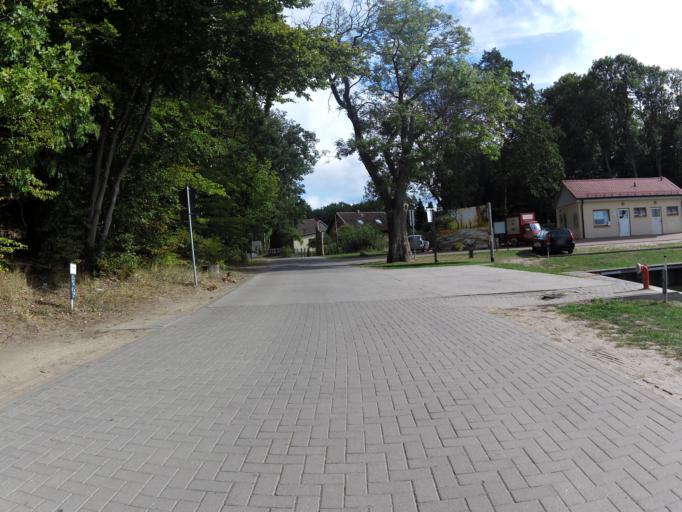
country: DE
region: Mecklenburg-Vorpommern
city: Loddin
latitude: 54.0014
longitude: 14.0472
